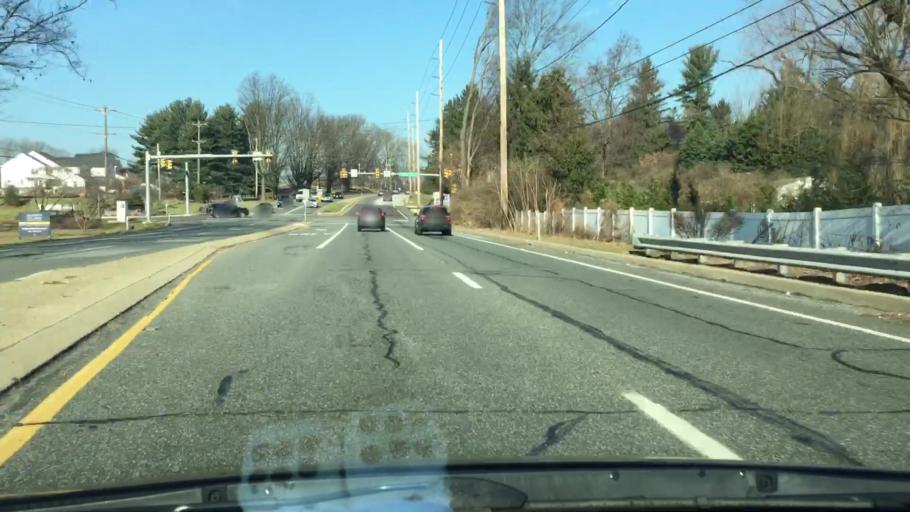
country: US
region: Pennsylvania
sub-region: Delaware County
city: Broomall
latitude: 39.9927
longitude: -75.4053
